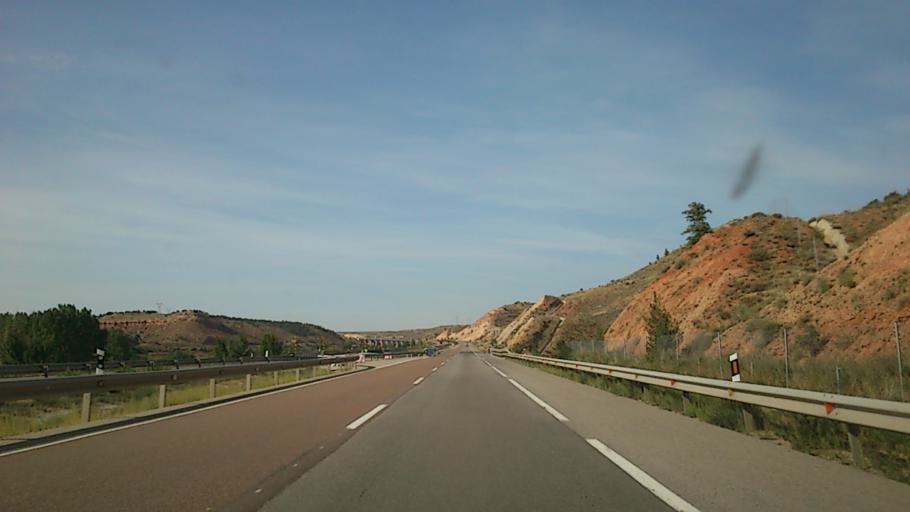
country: ES
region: Aragon
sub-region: Provincia de Teruel
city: Calamocha
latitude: 40.9780
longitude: -1.2597
